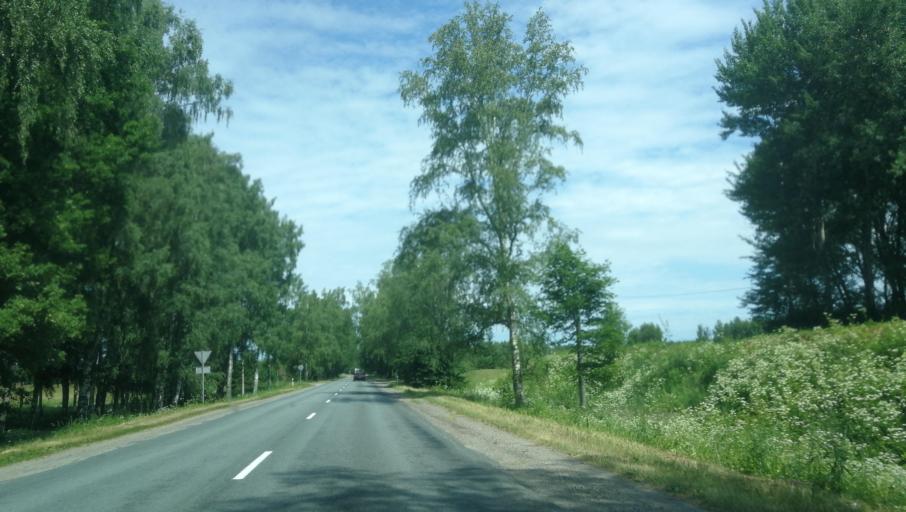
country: LV
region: Valmieras Rajons
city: Valmiera
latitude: 57.5588
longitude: 25.4388
